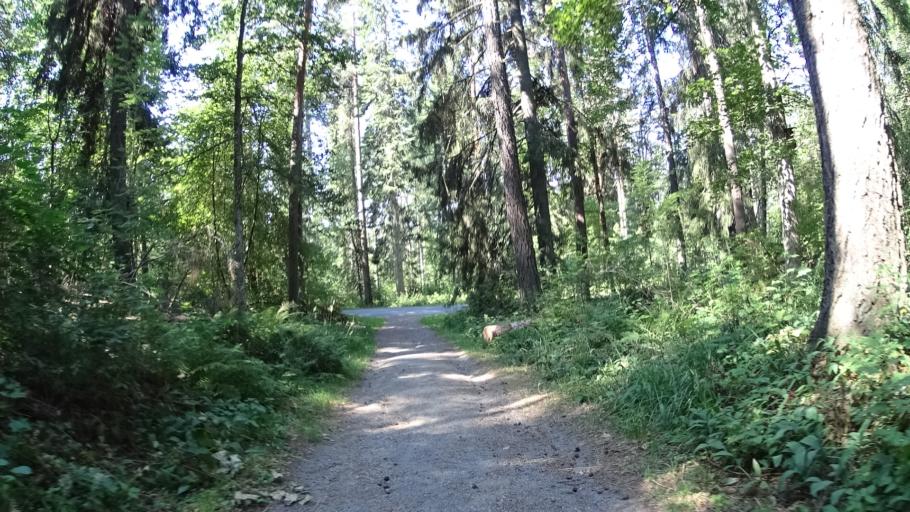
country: FI
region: Haeme
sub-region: Haemeenlinna
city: Haemeenlinna
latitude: 61.0226
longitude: 24.4502
